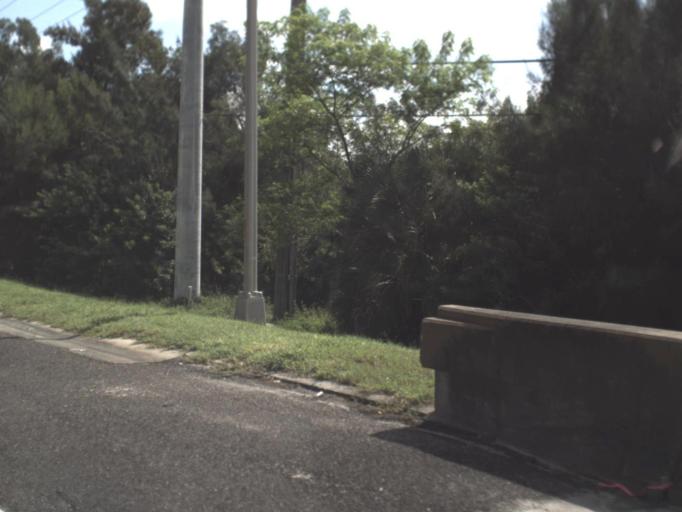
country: US
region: Florida
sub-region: Sarasota County
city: Warm Mineral Springs
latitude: 27.0461
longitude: -82.2911
